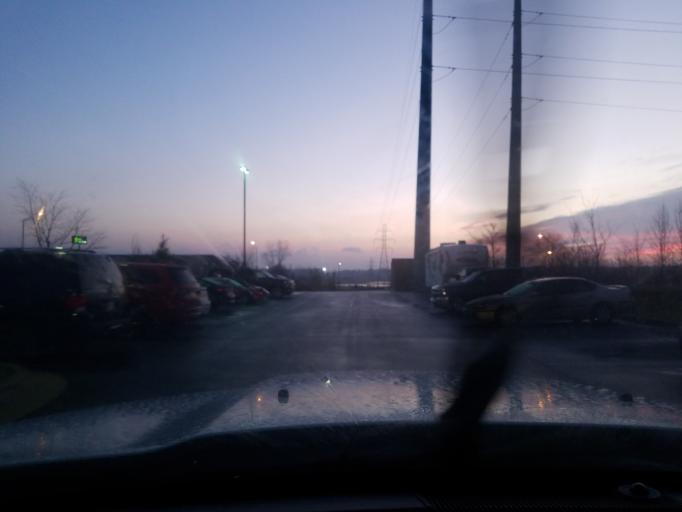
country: US
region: Indiana
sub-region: Huntington County
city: Roanoke
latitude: 41.0292
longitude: -85.2539
